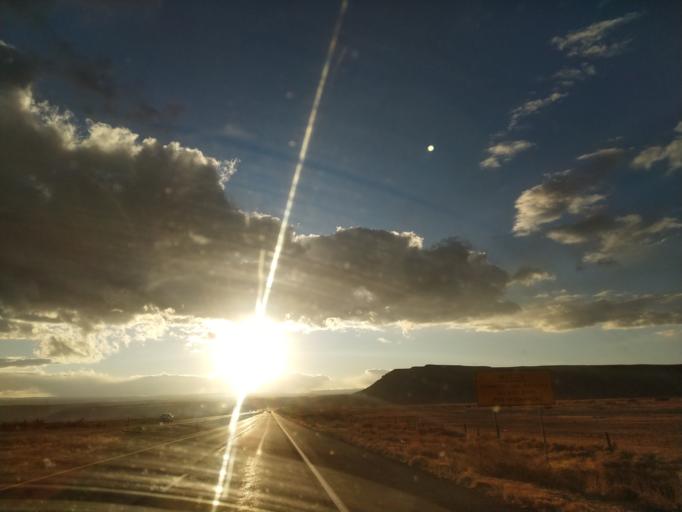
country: US
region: Colorado
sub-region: Delta County
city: Delta
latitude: 38.7567
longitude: -108.1488
